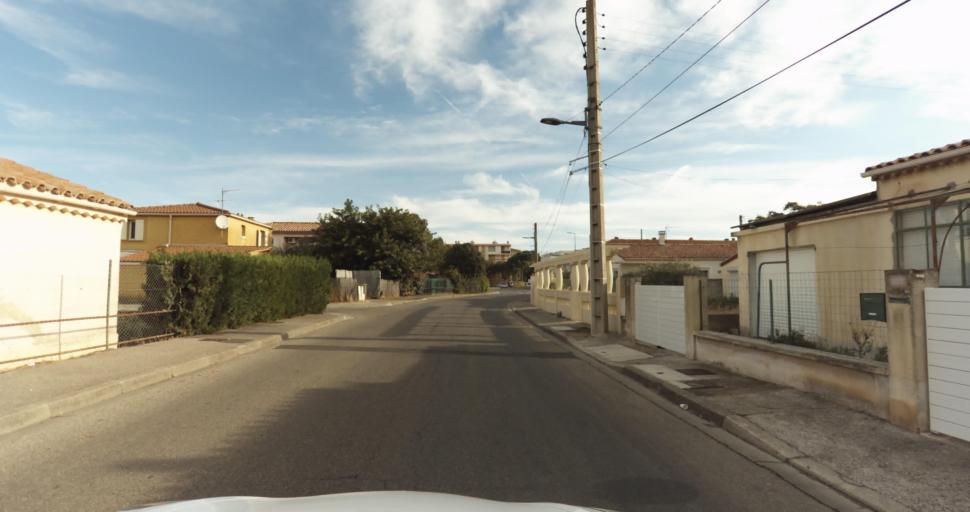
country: FR
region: Provence-Alpes-Cote d'Azur
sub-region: Departement des Bouches-du-Rhone
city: Miramas
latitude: 43.5857
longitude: 5.0001
